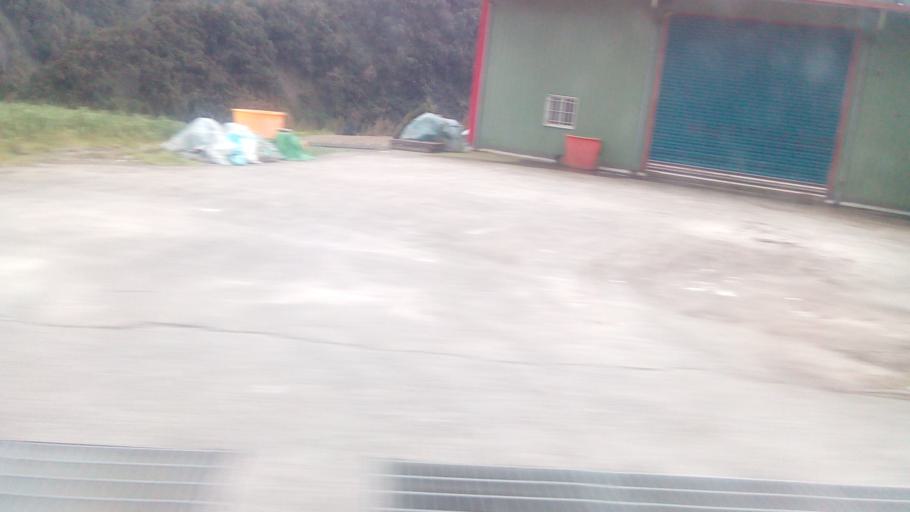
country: TW
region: Taiwan
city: Daxi
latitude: 24.4681
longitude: 121.4057
